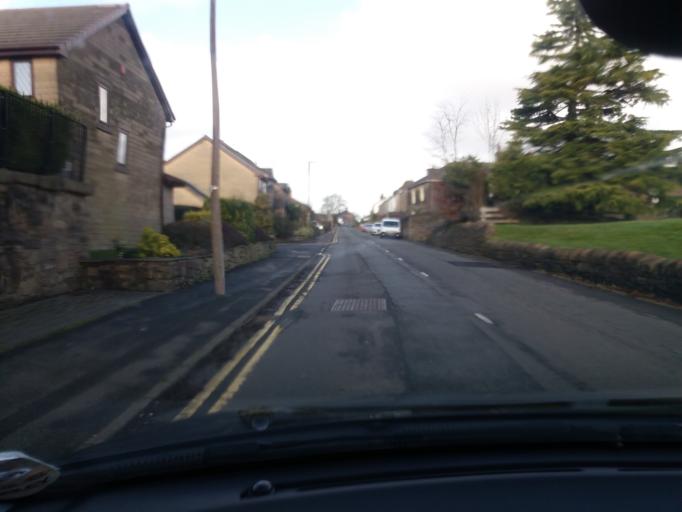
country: GB
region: England
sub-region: Lancashire
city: Adlington
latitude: 53.6216
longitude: -2.5918
